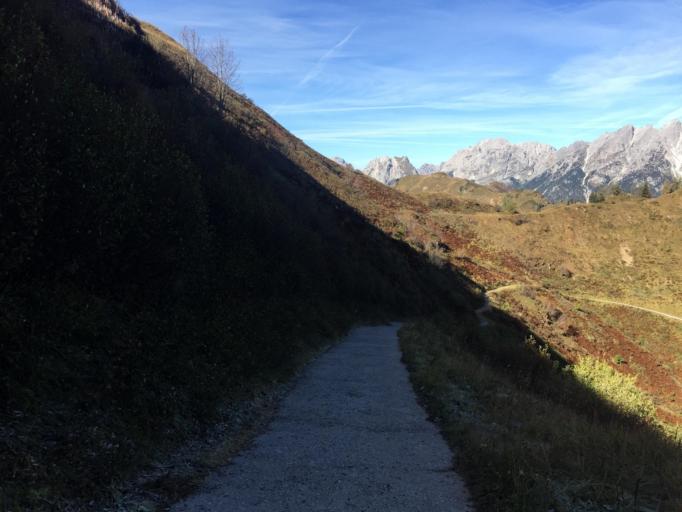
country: IT
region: Friuli Venezia Giulia
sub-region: Provincia di Udine
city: Sauris di Sotto
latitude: 46.4905
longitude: 12.7309
